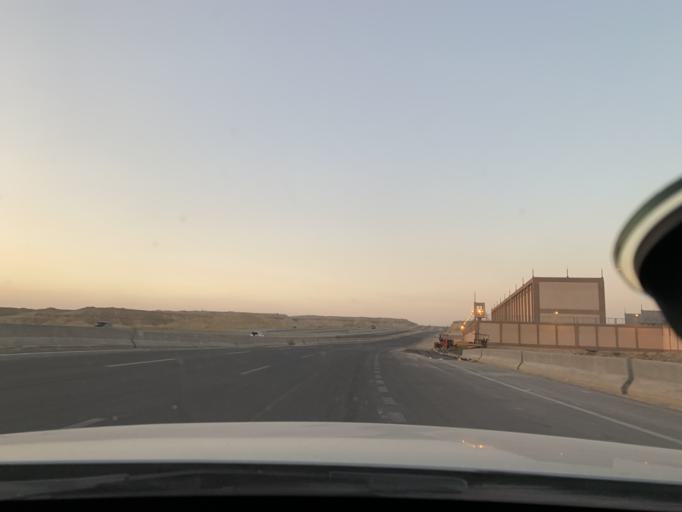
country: EG
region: Muhafazat al Qahirah
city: Halwan
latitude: 29.9372
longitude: 31.5293
